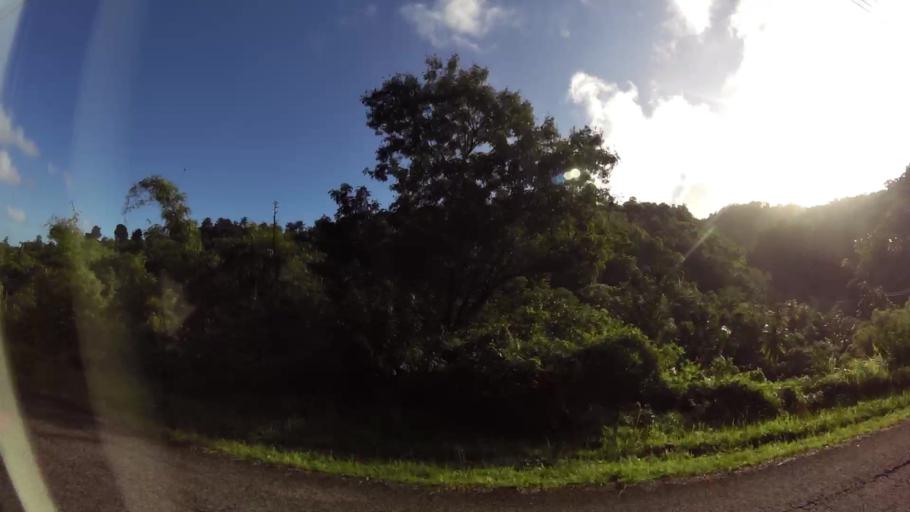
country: LC
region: Anse-la-Raye
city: Canaries
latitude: 13.9147
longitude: -61.0484
